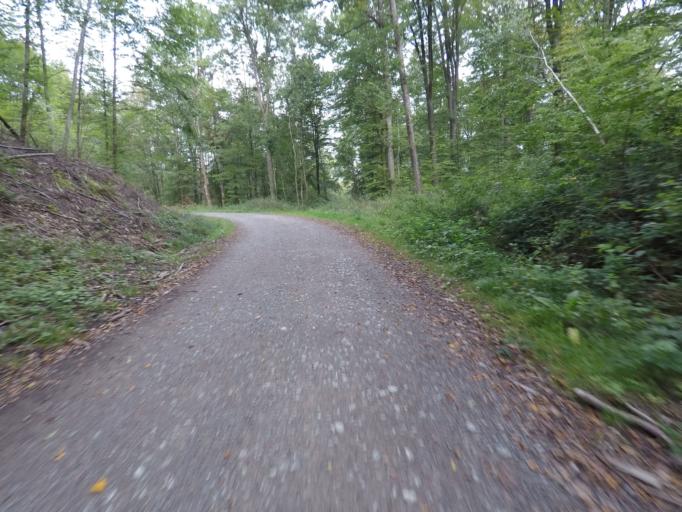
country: DE
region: Baden-Wuerttemberg
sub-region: Regierungsbezirk Stuttgart
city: Boeblingen
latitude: 48.6683
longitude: 8.9819
